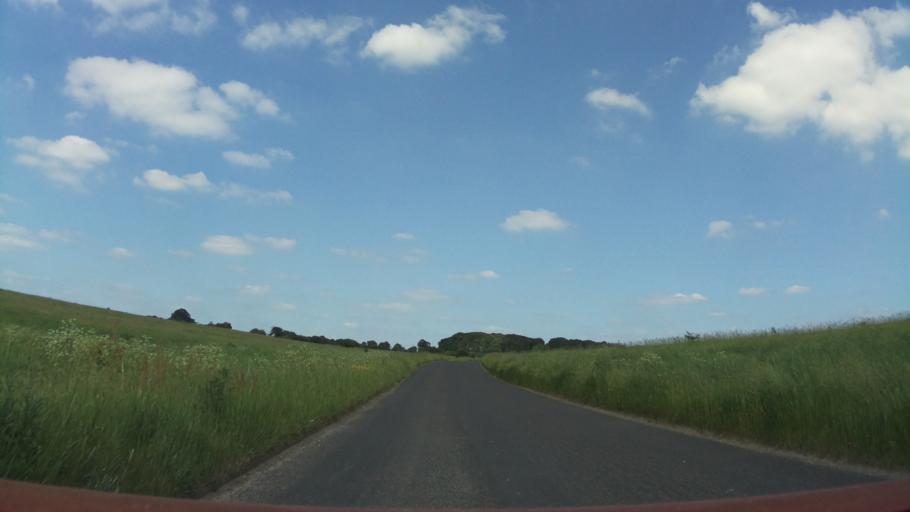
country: GB
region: England
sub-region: Wiltshire
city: Tidworth
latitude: 51.2694
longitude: -1.7160
